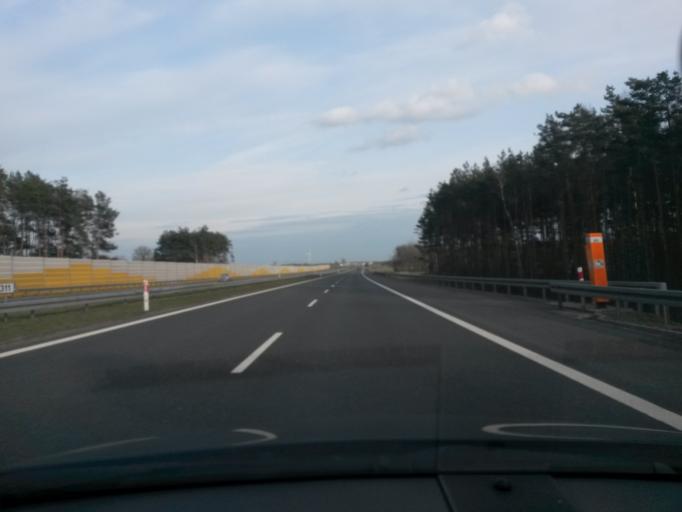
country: PL
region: Lodz Voivodeship
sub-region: Powiat leczycki
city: Swinice Warckie
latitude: 52.0249
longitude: 18.9193
